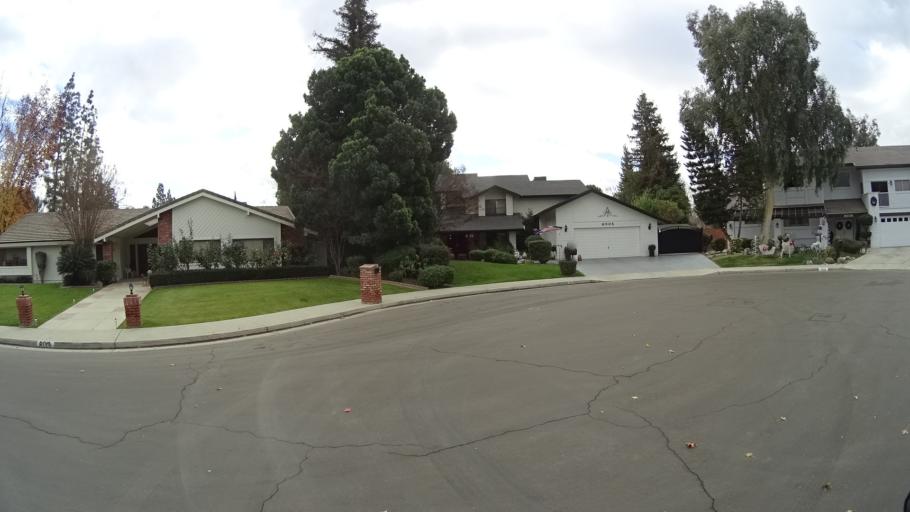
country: US
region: California
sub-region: Kern County
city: Greenacres
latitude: 35.3517
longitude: -119.0915
